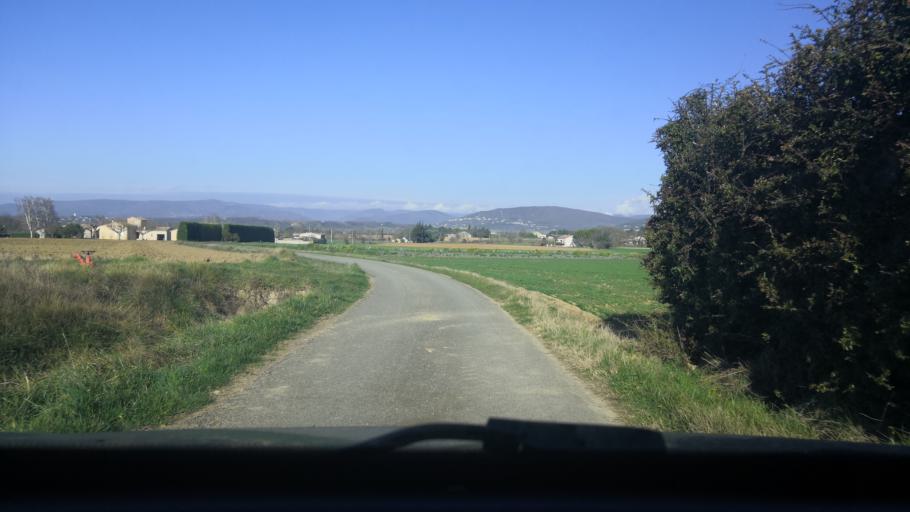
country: FR
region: Rhone-Alpes
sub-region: Departement de la Drome
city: Sauzet
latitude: 44.5710
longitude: 4.8421
